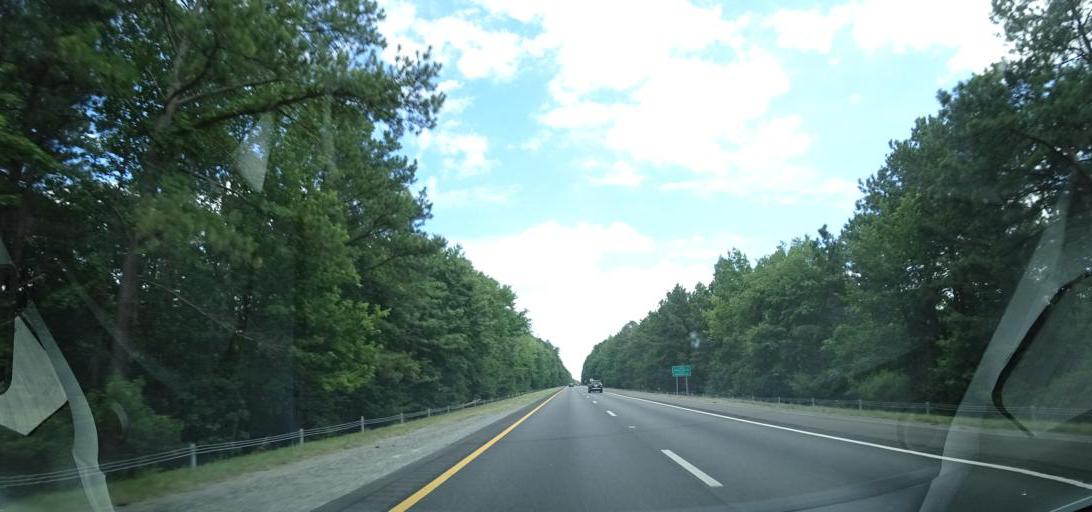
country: US
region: Virginia
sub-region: King William County
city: West Point
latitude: 37.4462
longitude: -76.8620
